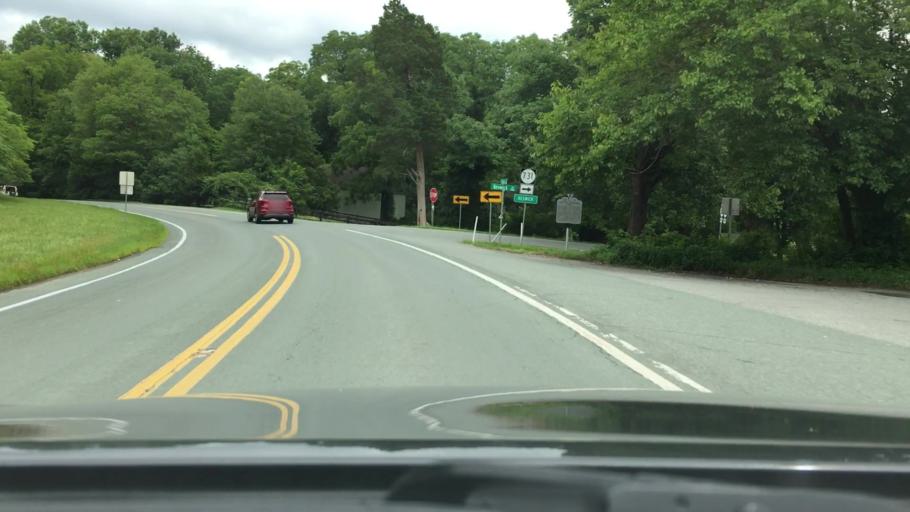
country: US
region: Virginia
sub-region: Fluvanna County
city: Lake Monticello
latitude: 38.0233
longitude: -78.3583
